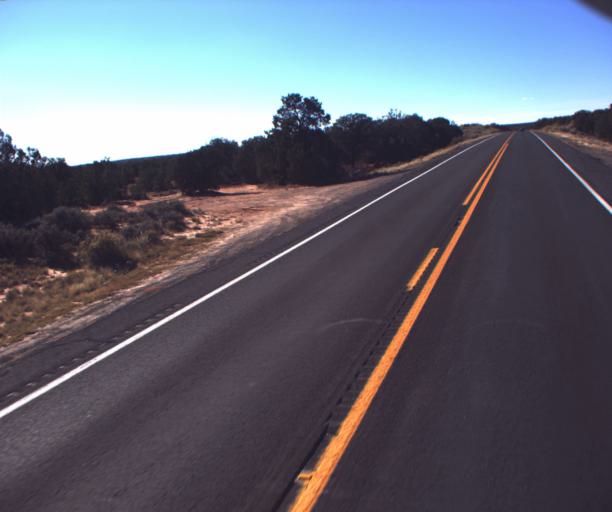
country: US
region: Arizona
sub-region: Coconino County
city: Kaibito
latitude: 36.5826
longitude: -110.8058
